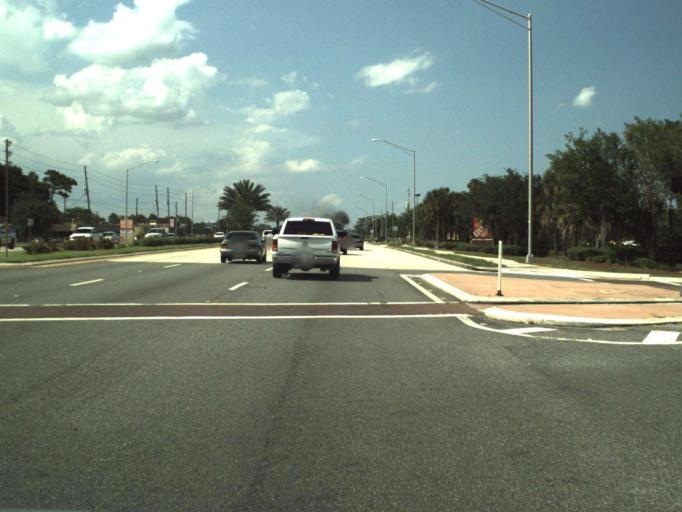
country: US
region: Florida
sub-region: Seminole County
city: Casselberry
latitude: 28.6761
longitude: -81.3365
